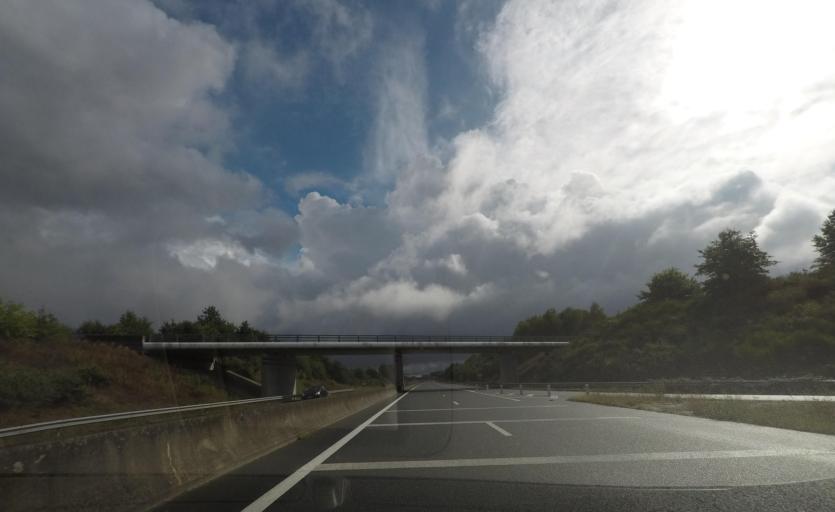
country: FR
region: Pays de la Loire
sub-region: Departement de la Vendee
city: La Ferriere
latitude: 46.6700
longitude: -1.3537
